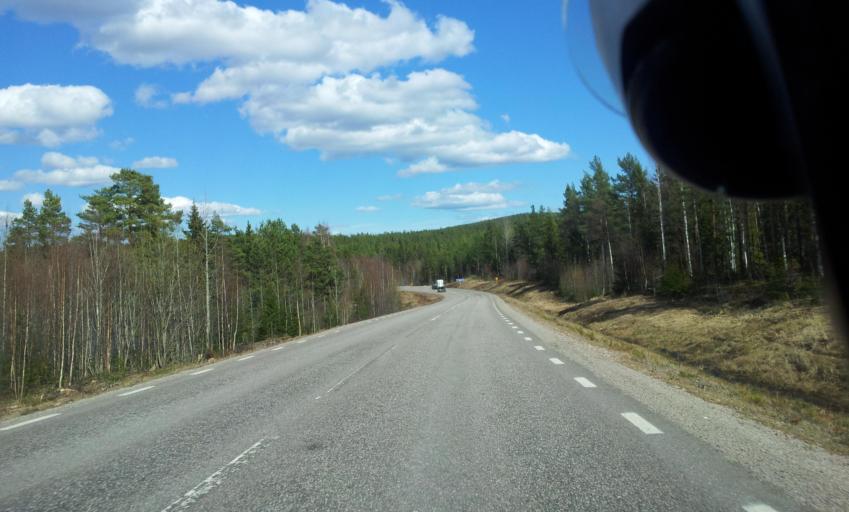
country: SE
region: Gaevleborg
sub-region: Ovanakers Kommun
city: Edsbyn
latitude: 61.2477
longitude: 15.8882
